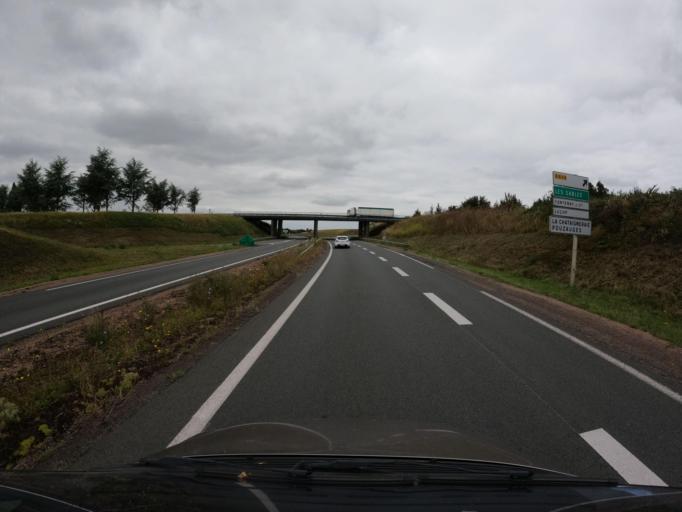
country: FR
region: Pays de la Loire
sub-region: Departement de la Vendee
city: Fontenay-le-Comte
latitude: 46.4667
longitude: -0.8466
